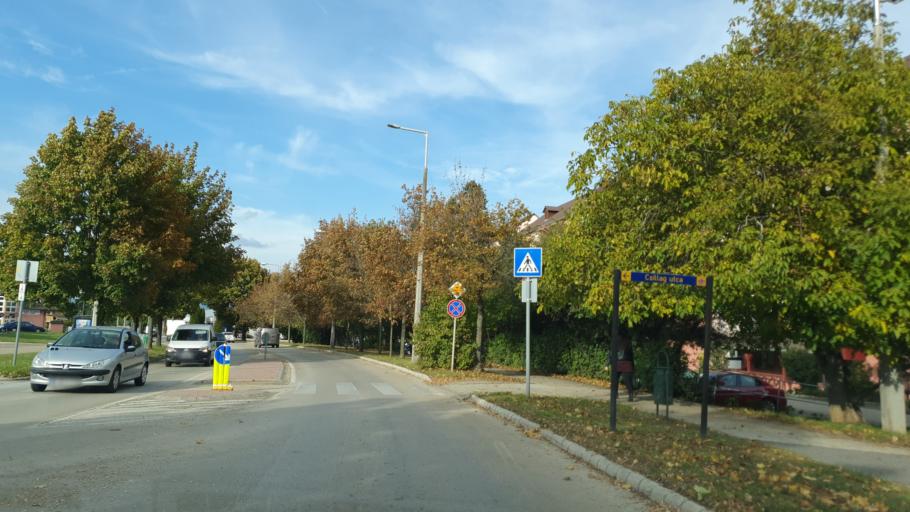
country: HU
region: Veszprem
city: Veszprem
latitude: 47.0960
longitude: 17.9275
